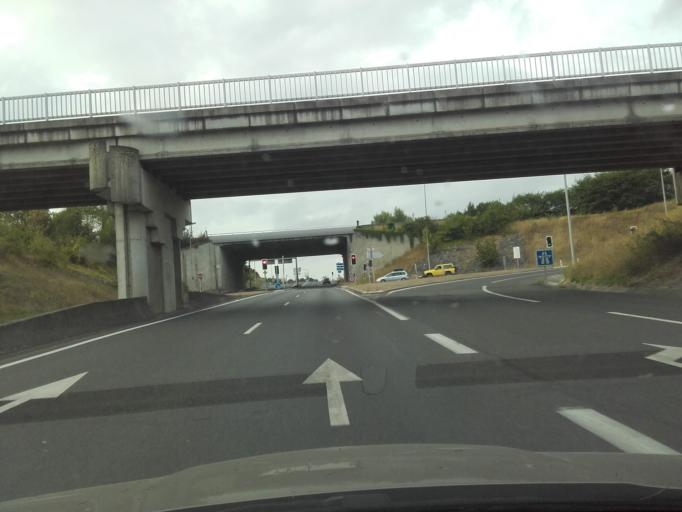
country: FR
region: Centre
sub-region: Departement d'Indre-et-Loire
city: Saint-Pierre-des-Corps
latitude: 47.4068
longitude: 0.7216
